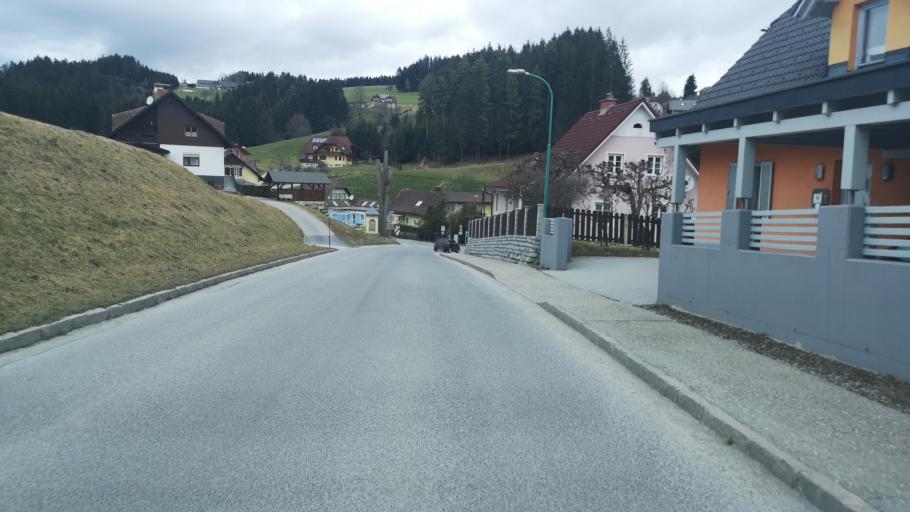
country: AT
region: Styria
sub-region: Politischer Bezirk Weiz
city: Birkfeld
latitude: 47.3579
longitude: 15.6907
